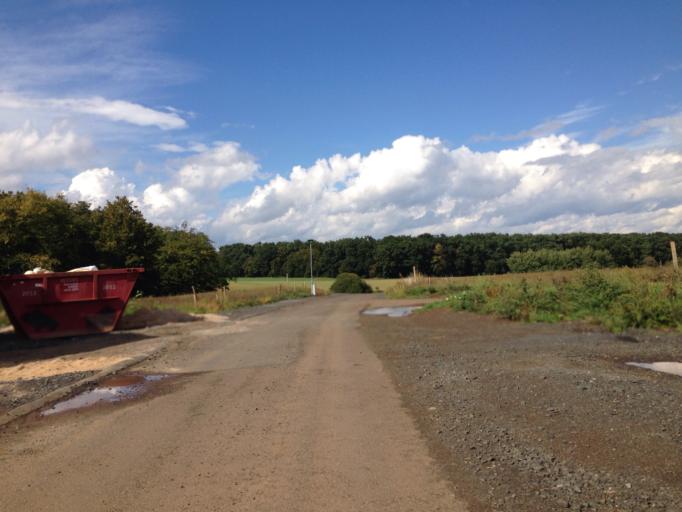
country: DE
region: Hesse
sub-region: Regierungsbezirk Giessen
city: Hungen
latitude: 50.4811
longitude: 8.8939
